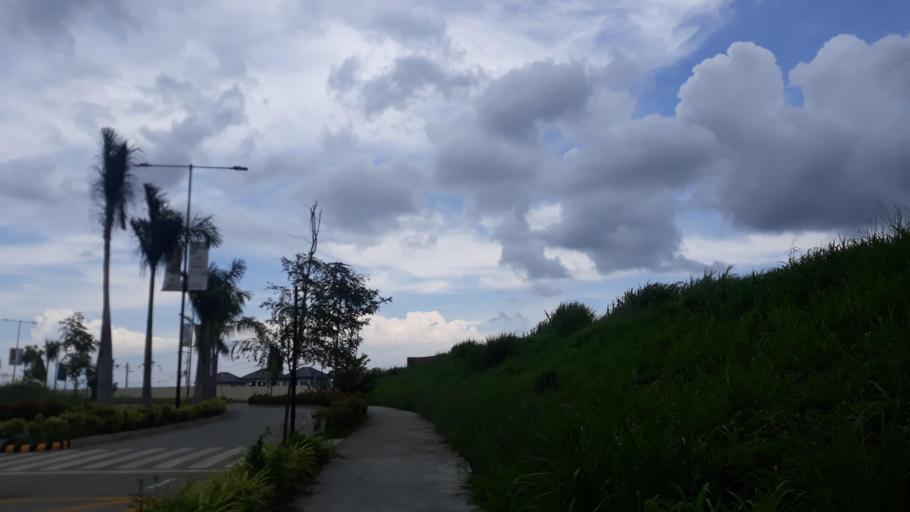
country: PH
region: Calabarzon
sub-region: Province of Cavite
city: Dasmarinas
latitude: 14.3035
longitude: 120.9502
